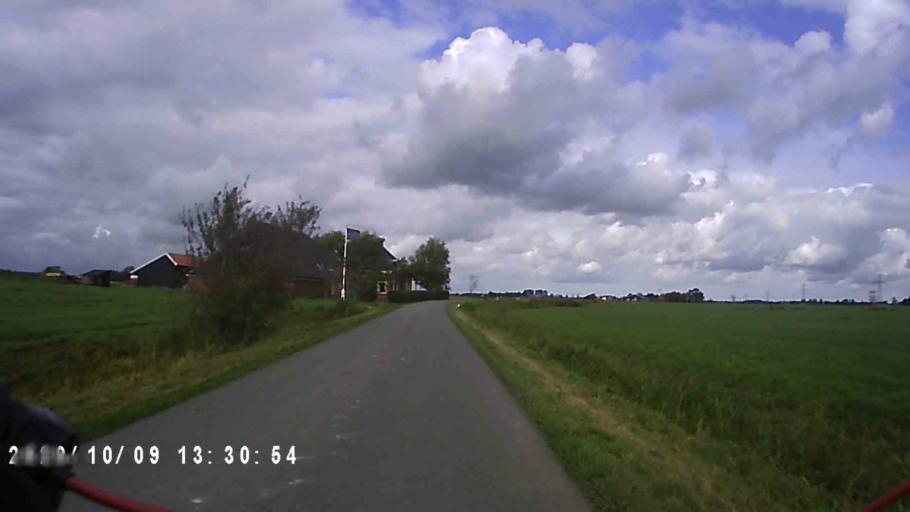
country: NL
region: Groningen
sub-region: Gemeente Zuidhorn
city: Aduard
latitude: 53.2779
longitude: 6.4719
